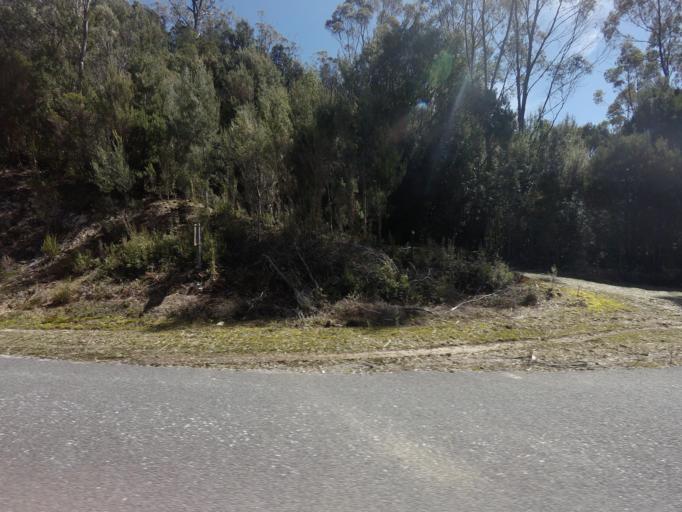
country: AU
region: Tasmania
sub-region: West Coast
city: Queenstown
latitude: -42.7561
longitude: 145.9940
